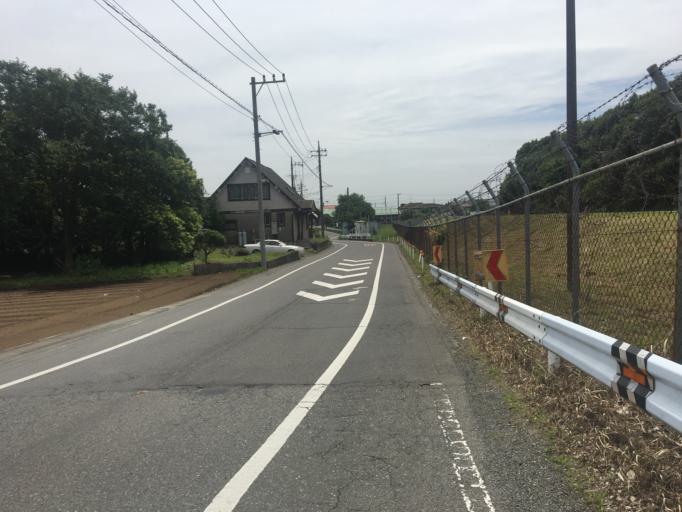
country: JP
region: Saitama
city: Sayama
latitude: 35.8353
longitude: 139.4170
